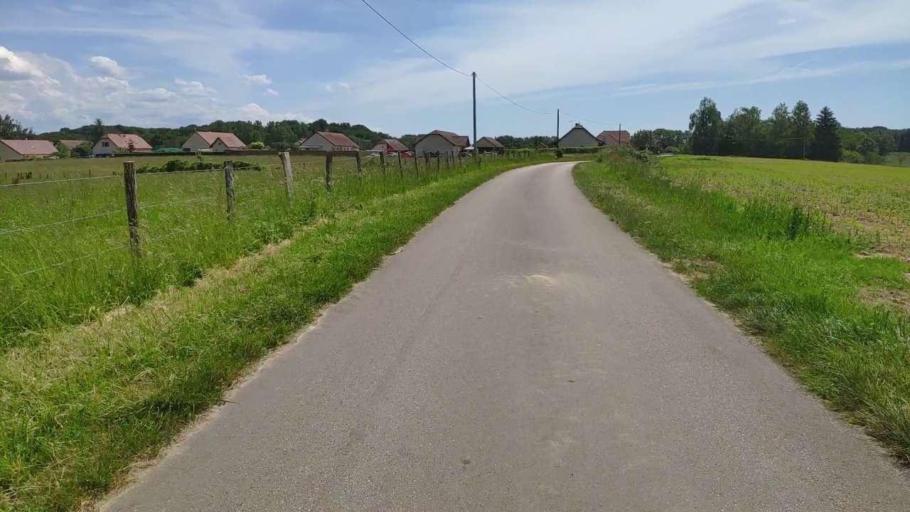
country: FR
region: Franche-Comte
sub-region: Departement du Jura
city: Bletterans
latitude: 46.7681
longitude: 5.4320
